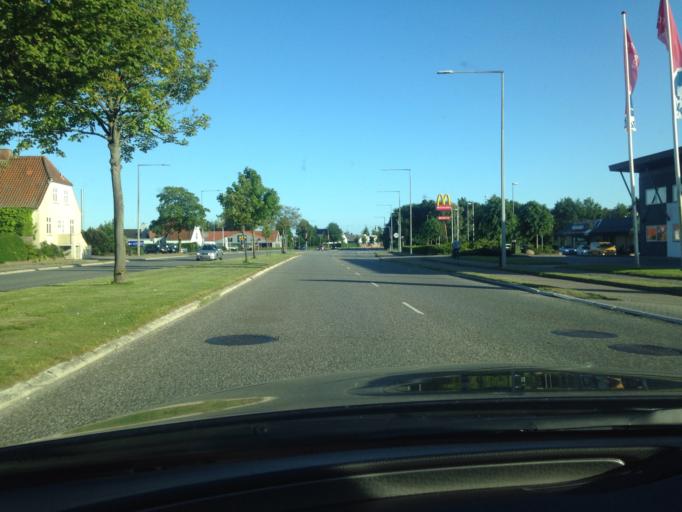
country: DK
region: South Denmark
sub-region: Kolding Kommune
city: Kolding
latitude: 55.5051
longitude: 9.4577
